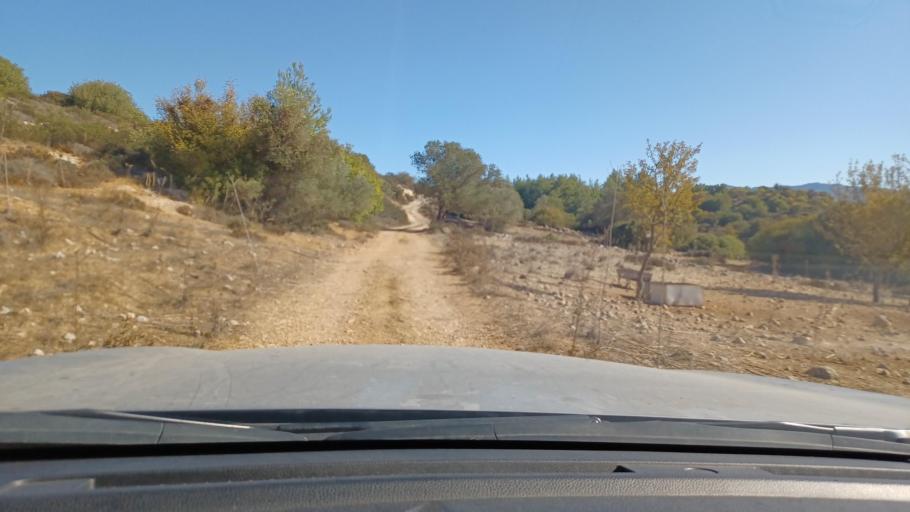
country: CY
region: Pafos
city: Polis
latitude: 34.9893
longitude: 32.5204
